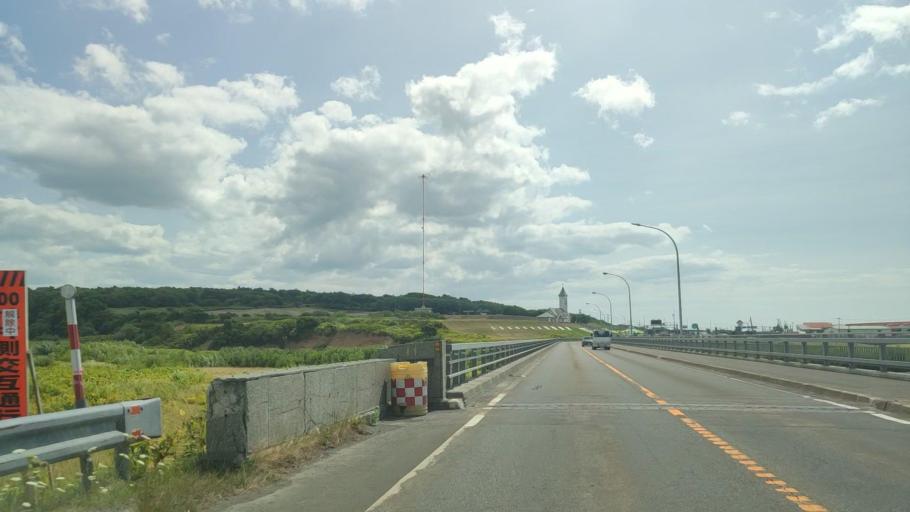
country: JP
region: Hokkaido
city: Makubetsu
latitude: 44.7184
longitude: 141.7933
